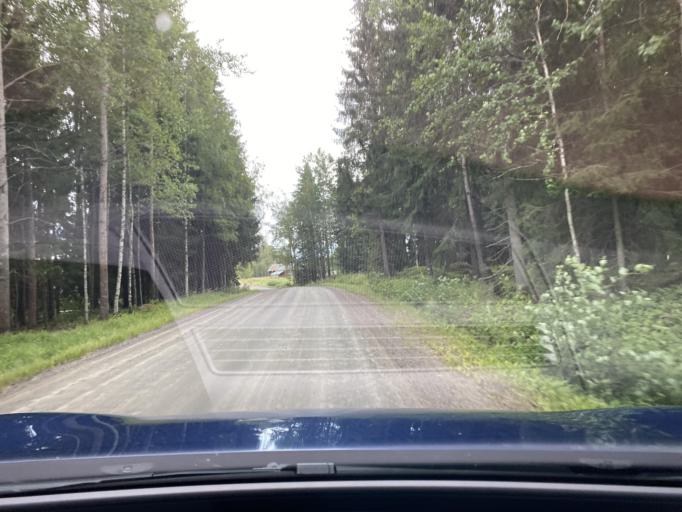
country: FI
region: Pirkanmaa
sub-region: Lounais-Pirkanmaa
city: Punkalaidun
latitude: 61.2183
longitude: 23.1660
